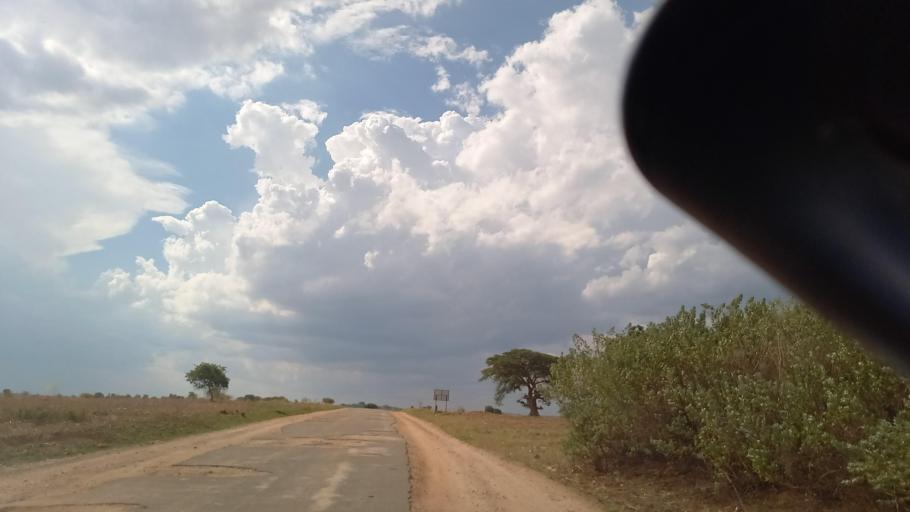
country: ZM
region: Lusaka
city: Kafue
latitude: -16.2028
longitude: 28.1092
